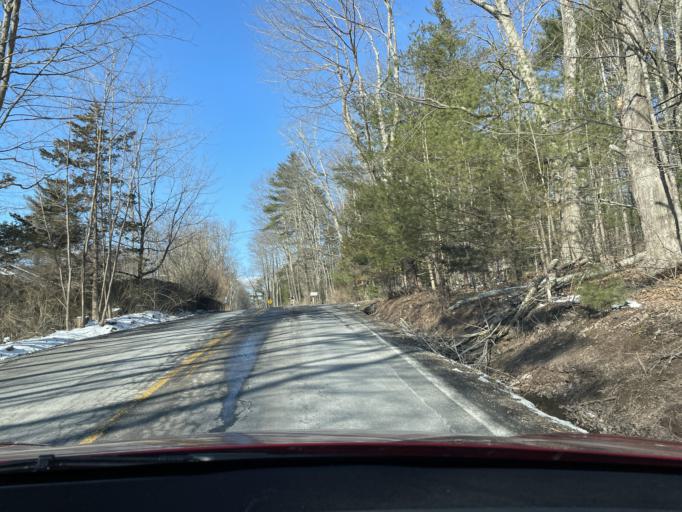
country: US
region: New York
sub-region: Ulster County
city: Woodstock
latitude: 42.0496
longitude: -74.1256
